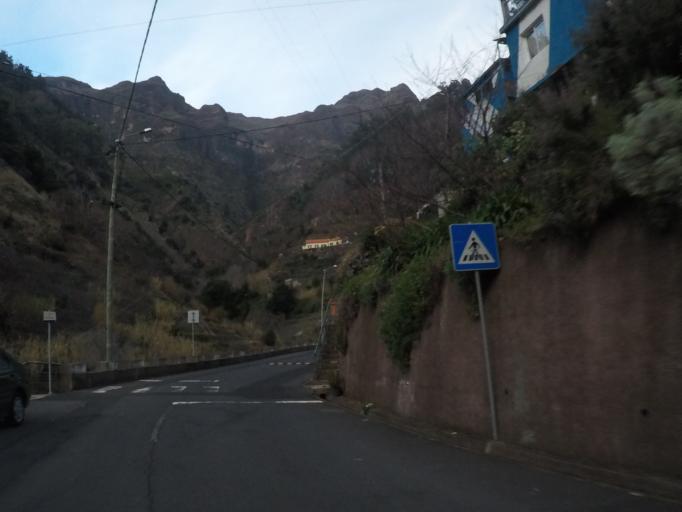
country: PT
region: Madeira
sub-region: Camara de Lobos
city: Curral das Freiras
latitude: 32.7438
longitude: -16.9647
